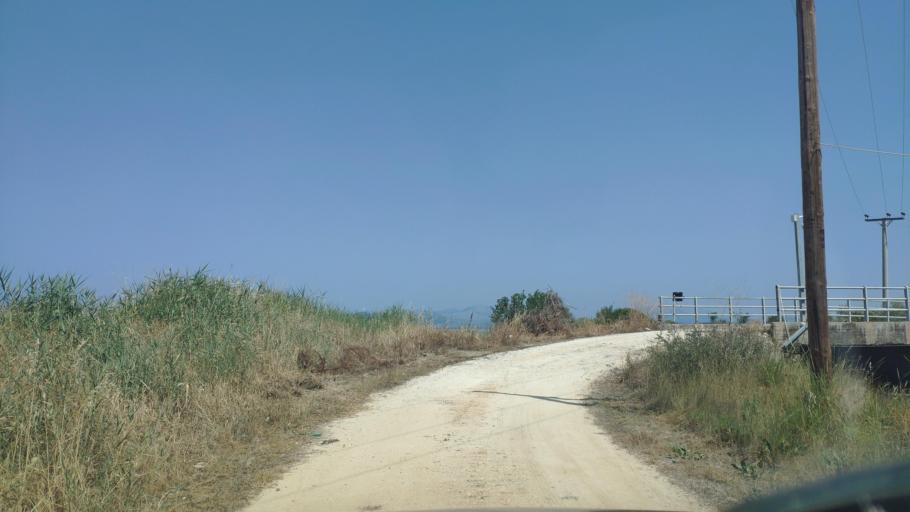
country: GR
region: Epirus
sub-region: Nomos Artas
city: Aneza
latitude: 39.0160
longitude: 20.9294
